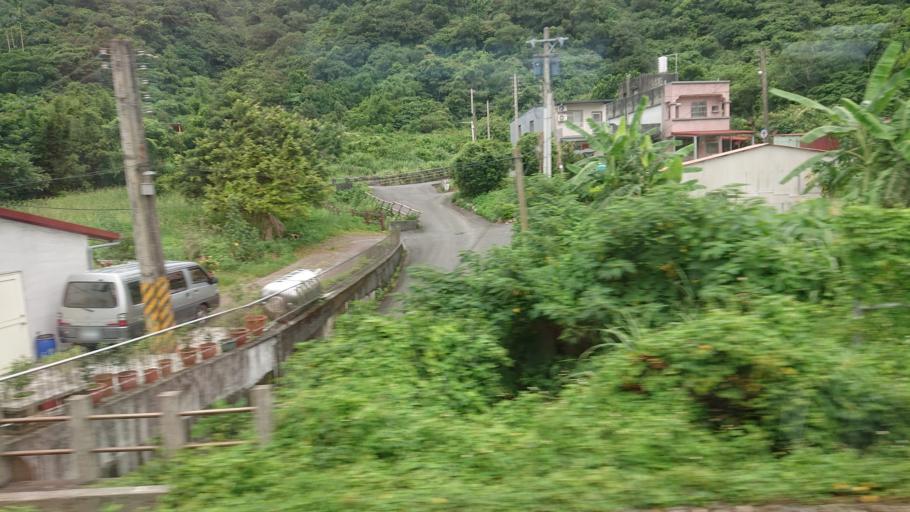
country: TW
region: Taiwan
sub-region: Yilan
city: Yilan
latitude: 24.9229
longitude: 121.8829
